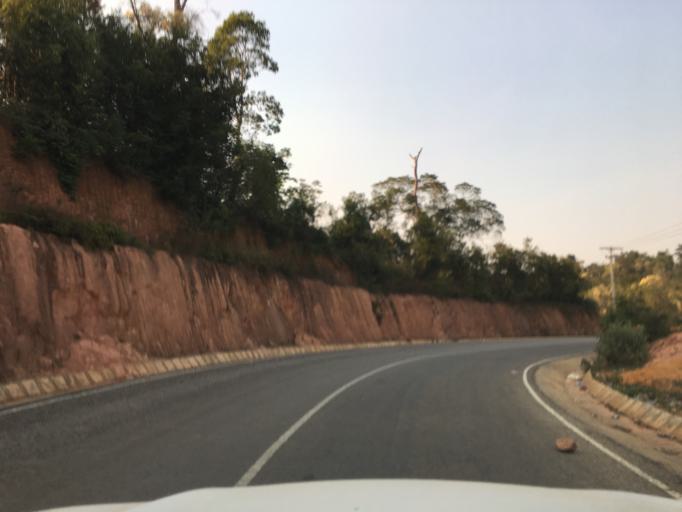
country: LA
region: Houaphan
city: Xam Nua
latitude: 20.6055
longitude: 104.0735
